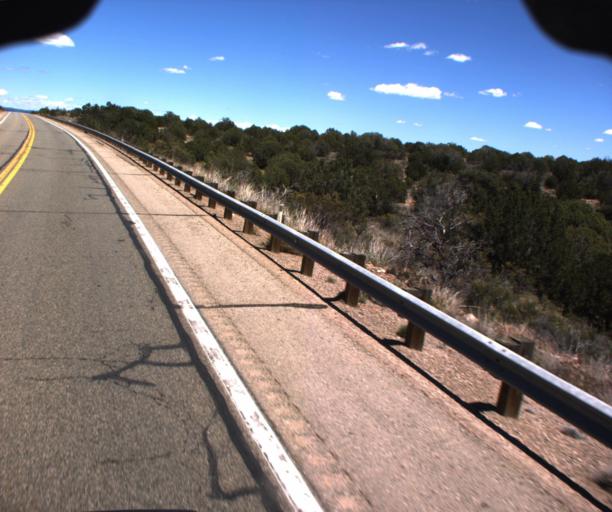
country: US
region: Arizona
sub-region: Yavapai County
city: Paulden
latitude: 34.9335
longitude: -112.4365
